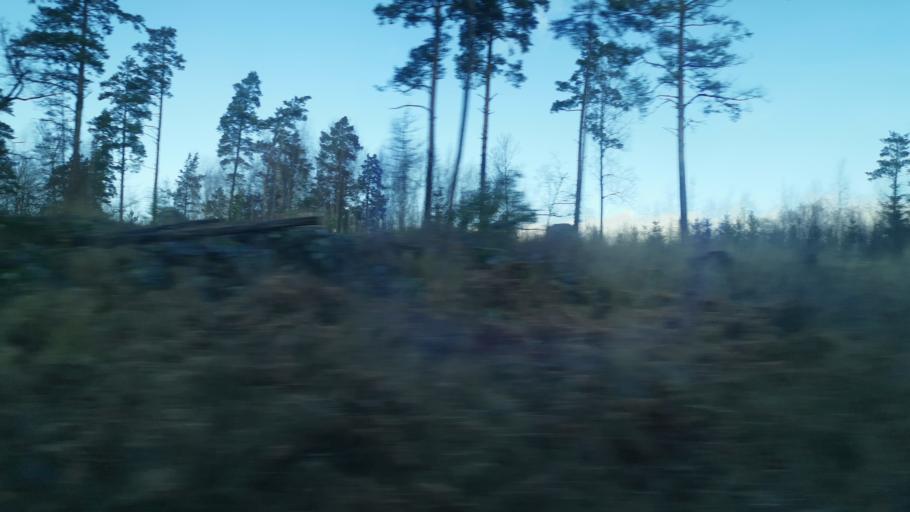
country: SE
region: Soedermanland
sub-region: Flens Kommun
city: Malmkoping
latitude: 59.0919
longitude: 16.9177
